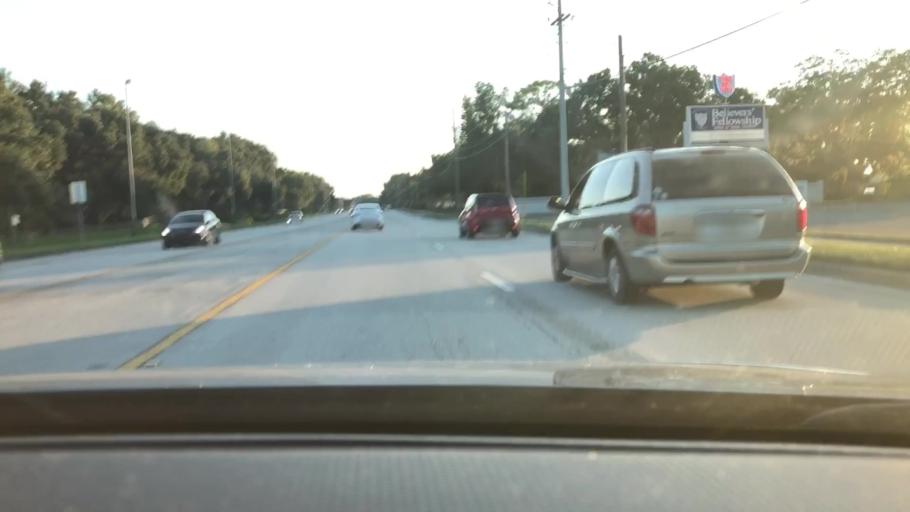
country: US
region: Florida
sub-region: Polk County
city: Gibsonia
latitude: 28.1093
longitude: -81.9473
